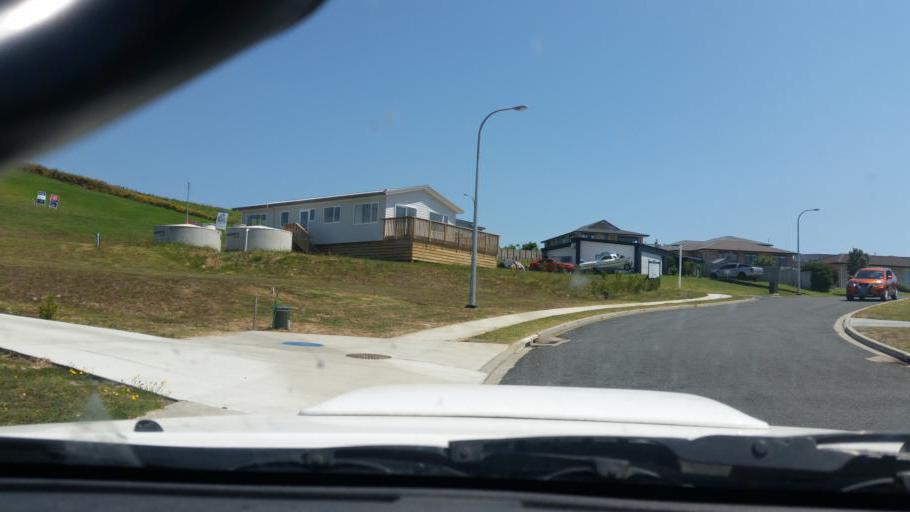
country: NZ
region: Auckland
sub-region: Auckland
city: Wellsford
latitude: -36.1253
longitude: 174.5710
